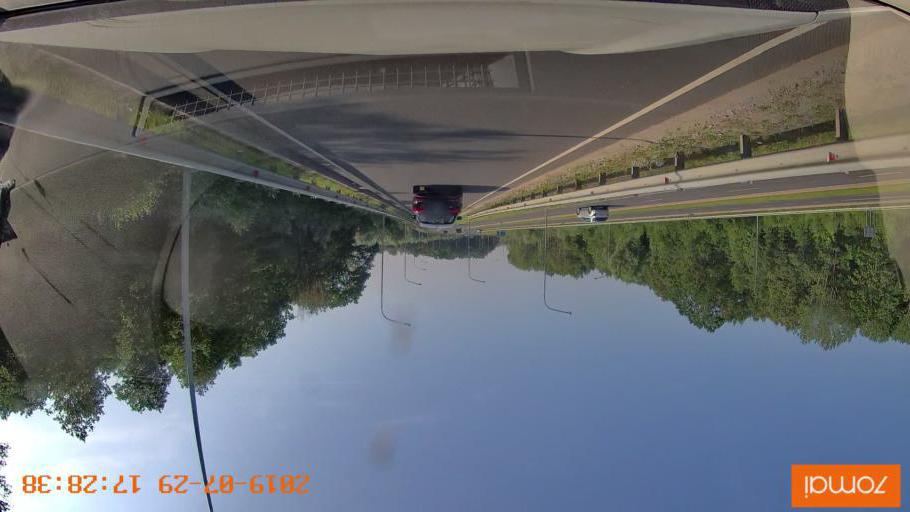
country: RU
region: Kaliningrad
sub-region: Gorod Kaliningrad
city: Kaliningrad
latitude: 54.7617
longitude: 20.4703
